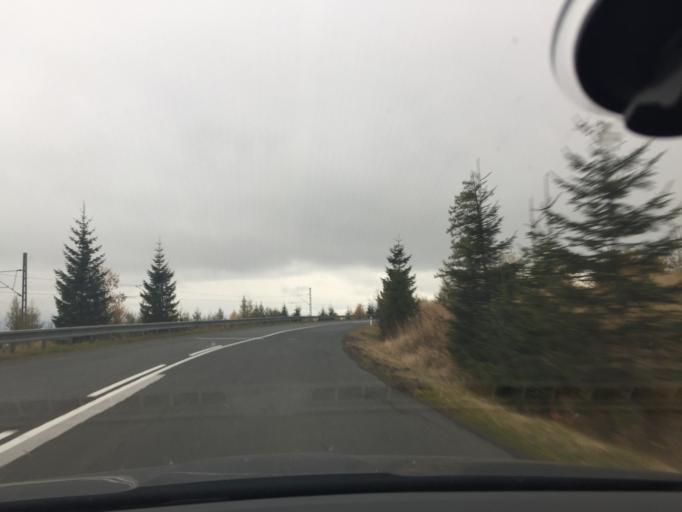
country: SK
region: Presovsky
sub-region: Okres Poprad
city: Vysoke Tatry
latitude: 49.1267
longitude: 20.1967
